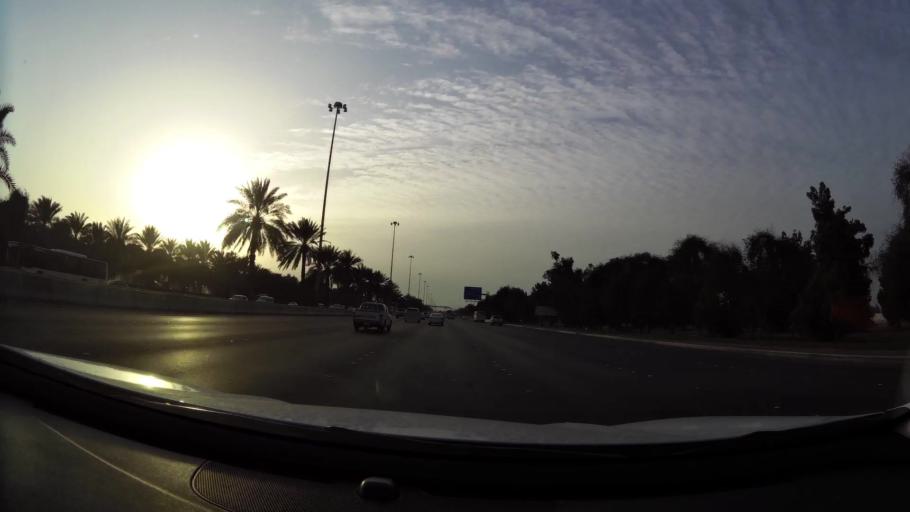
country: AE
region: Abu Dhabi
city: Abu Dhabi
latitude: 24.3974
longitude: 54.5083
